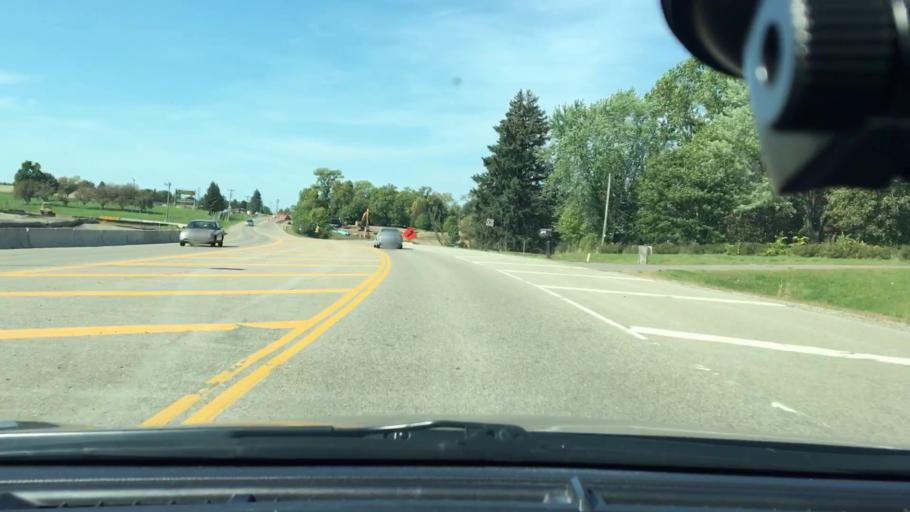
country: US
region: Minnesota
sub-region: Hennepin County
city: Corcoran
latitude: 45.0871
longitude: -93.5199
